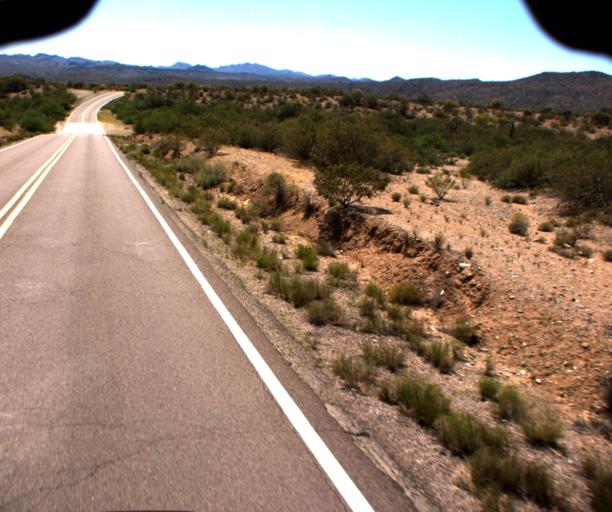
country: US
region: Arizona
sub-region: Yavapai County
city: Bagdad
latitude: 34.4716
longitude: -113.2138
